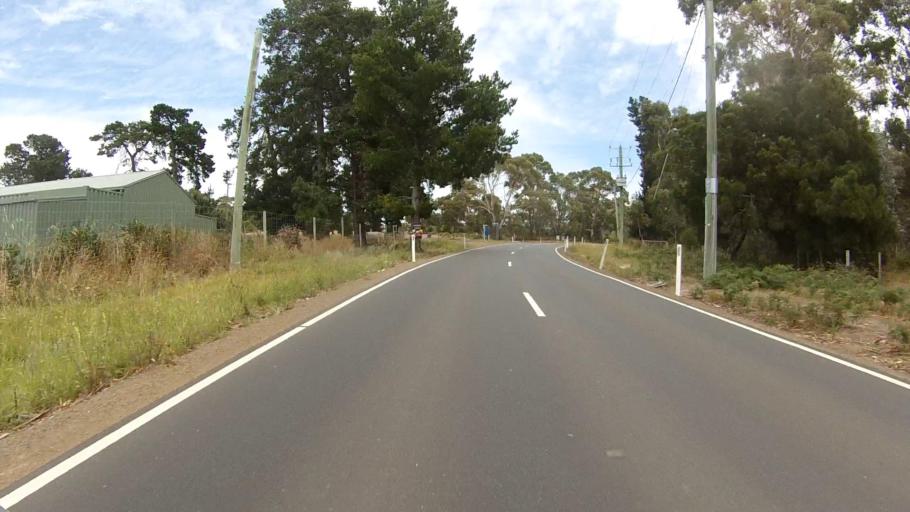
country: AU
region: Tasmania
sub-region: Clarence
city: Acton Park
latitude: -42.8672
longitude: 147.4876
